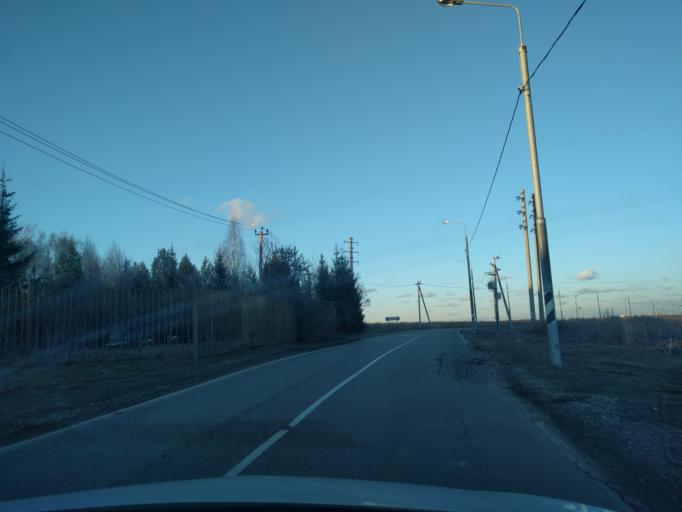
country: RU
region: Moskovskaya
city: Vatutinki
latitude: 55.4908
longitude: 37.4162
